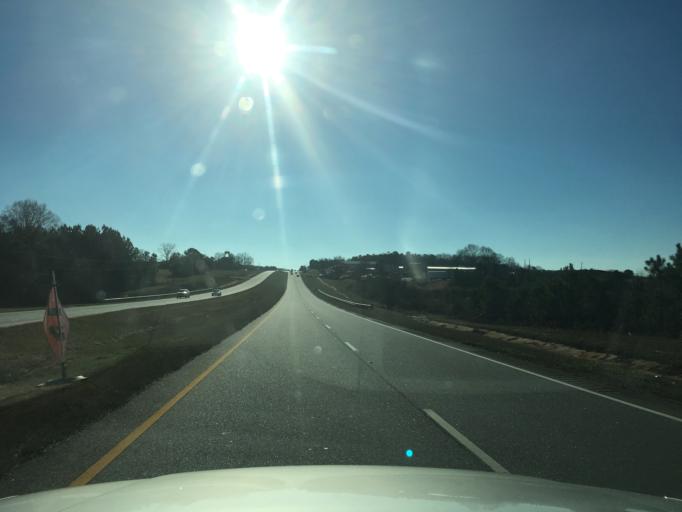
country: US
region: Georgia
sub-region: Carroll County
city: Carrollton
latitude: 33.4799
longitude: -85.1035
